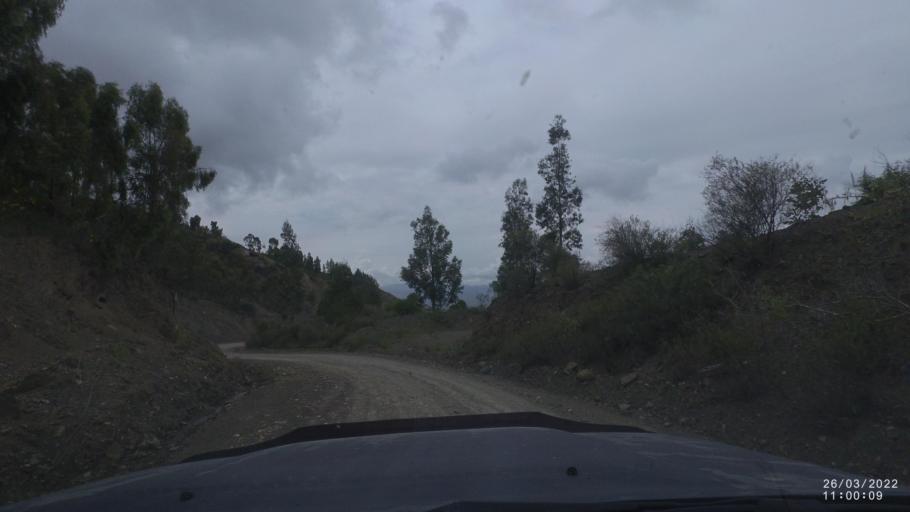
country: BO
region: Cochabamba
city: Tarata
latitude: -17.5143
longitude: -66.0242
